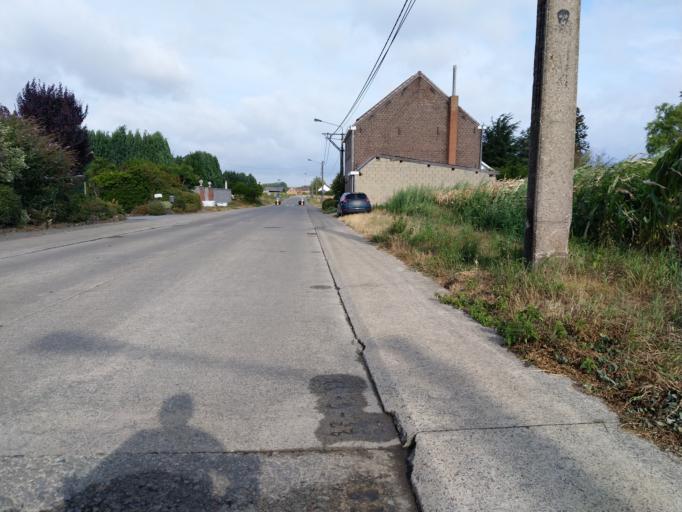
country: BE
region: Wallonia
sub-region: Province du Hainaut
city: Jurbise
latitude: 50.5295
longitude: 3.9010
